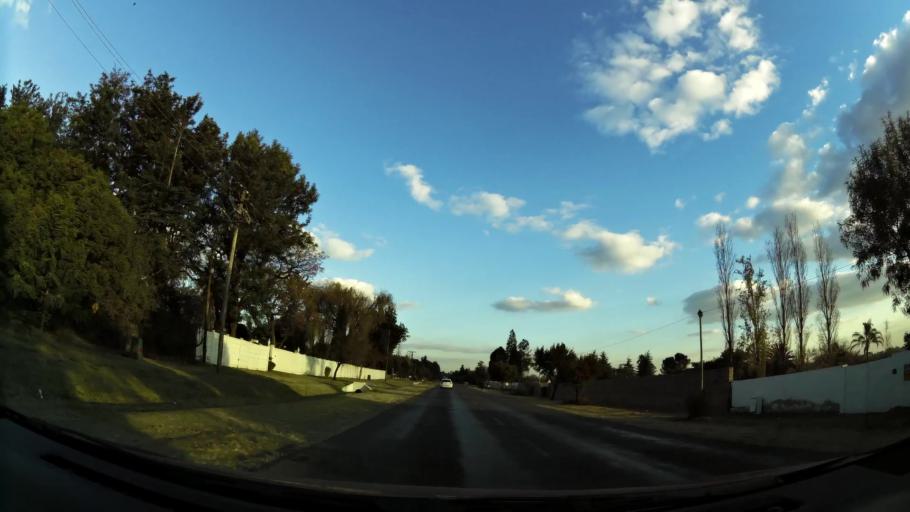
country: ZA
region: Gauteng
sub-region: City of Johannesburg Metropolitan Municipality
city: Midrand
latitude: -25.9754
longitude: 28.1532
